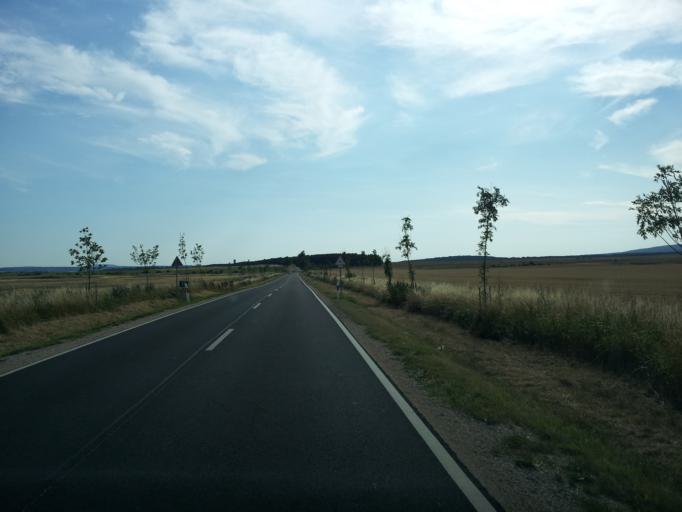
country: HU
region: Veszprem
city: Nemesvamos
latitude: 47.0158
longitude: 17.7706
